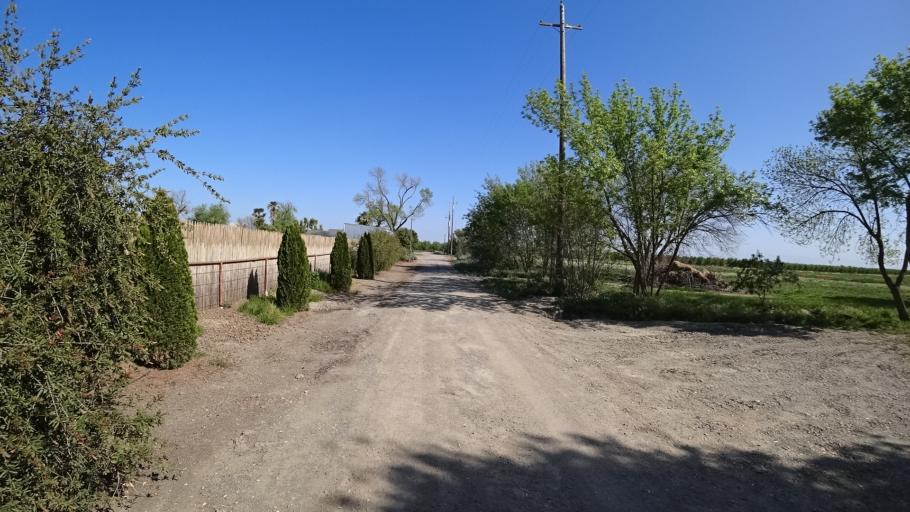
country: US
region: California
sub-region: Glenn County
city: Hamilton City
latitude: 39.6385
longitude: -122.0275
